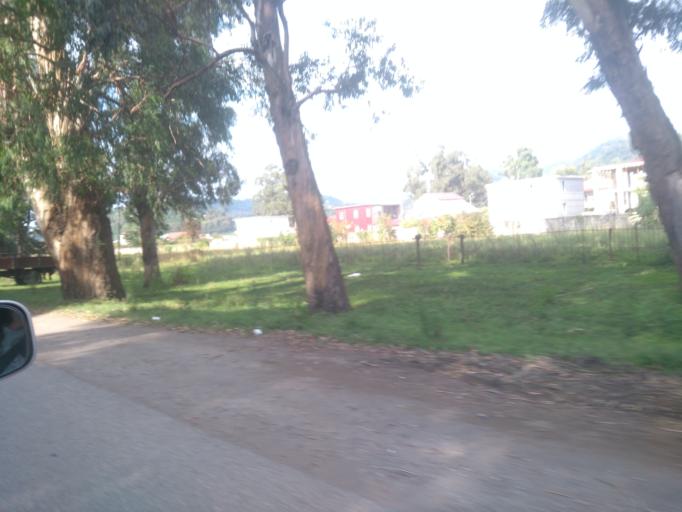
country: GE
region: Ajaria
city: Khelvachauri
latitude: 41.5845
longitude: 41.6527
